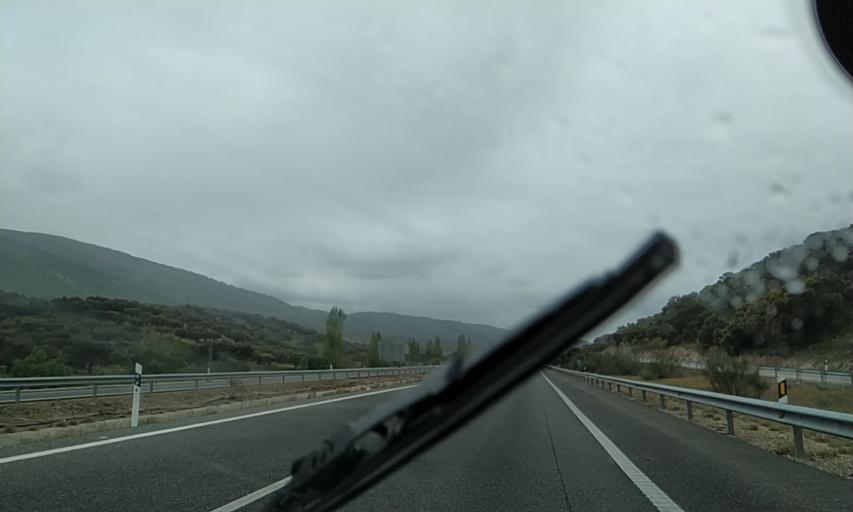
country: ES
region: Extremadura
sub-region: Provincia de Caceres
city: Villar de Plasencia
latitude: 40.1301
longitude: -6.0493
